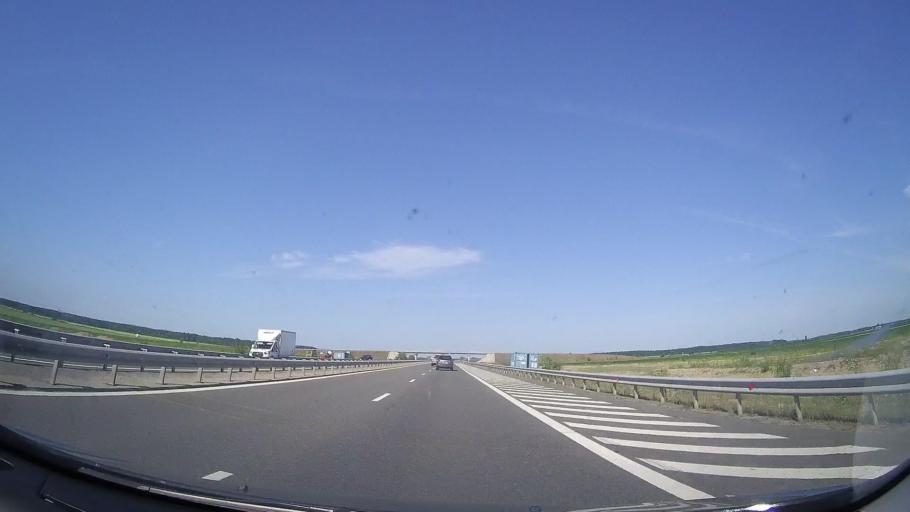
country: RO
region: Prahova
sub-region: Comuna Berceni
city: Corlatesti
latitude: 44.8858
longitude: 26.0931
